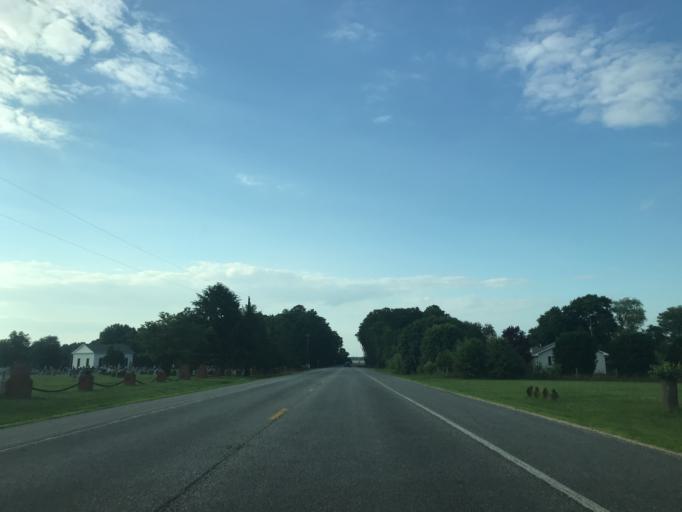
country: US
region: Maryland
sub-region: Caroline County
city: Denton
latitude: 38.7998
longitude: -75.7868
